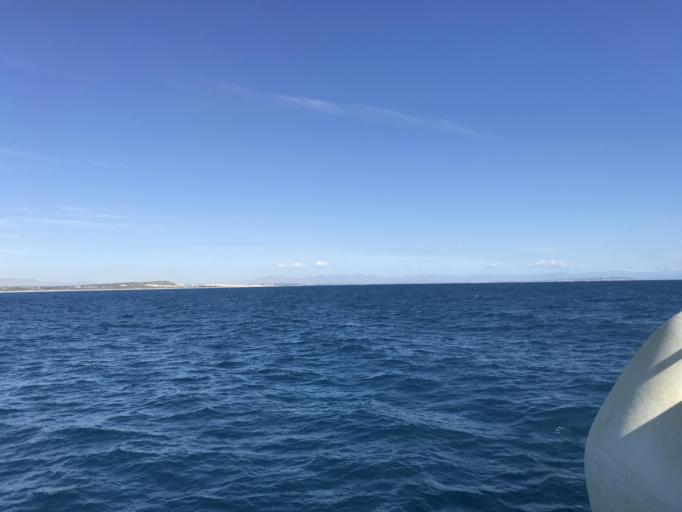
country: ES
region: Valencia
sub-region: Provincia de Alicante
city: Torrevieja
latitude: 38.0102
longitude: -0.6297
